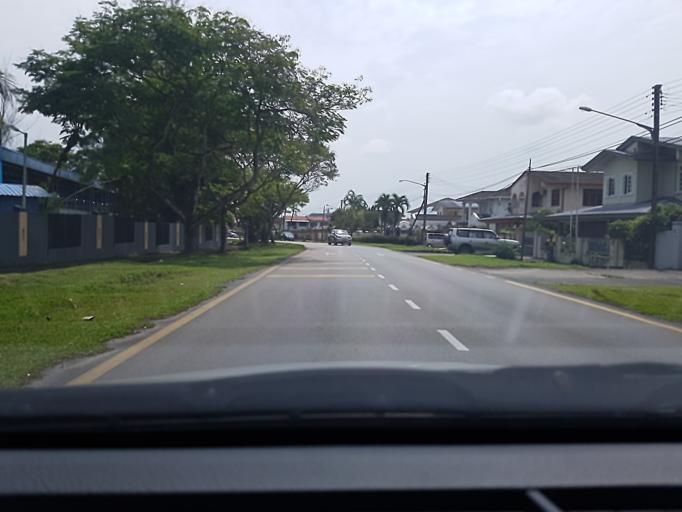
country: MY
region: Sarawak
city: Kuching
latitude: 1.5102
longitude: 110.3625
